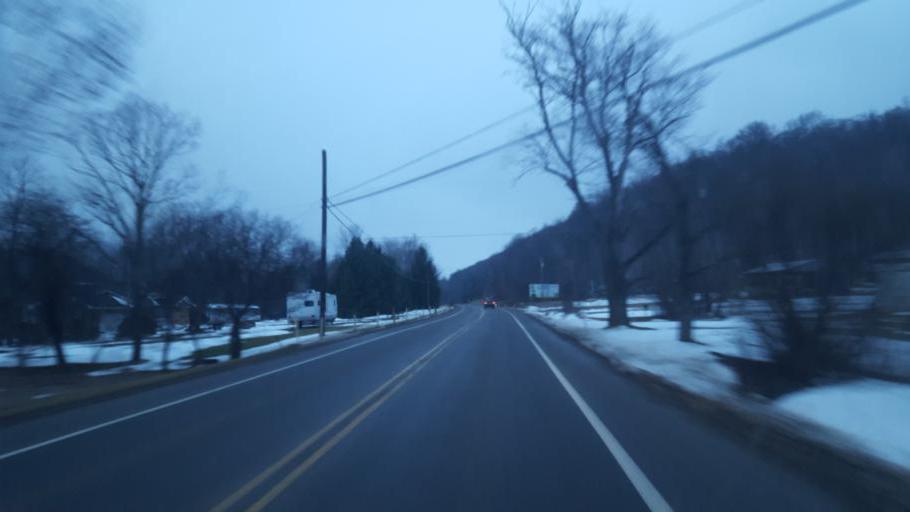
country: US
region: Pennsylvania
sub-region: Potter County
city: Coudersport
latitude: 41.7480
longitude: -78.0942
